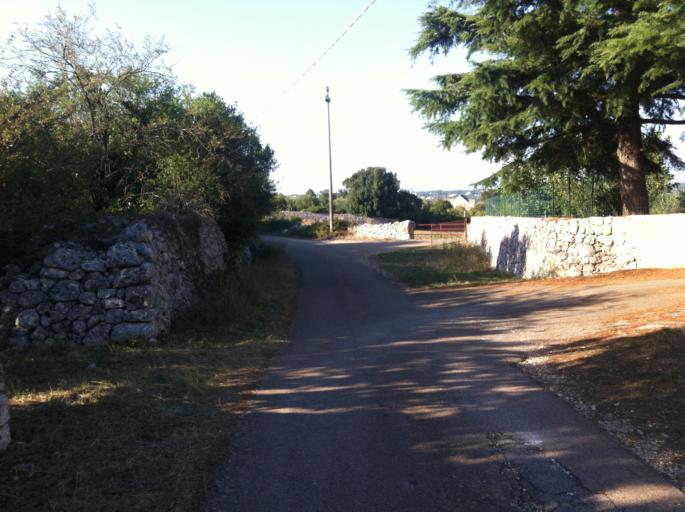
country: IT
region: Apulia
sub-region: Provincia di Bari
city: Noci
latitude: 40.8230
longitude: 17.1397
